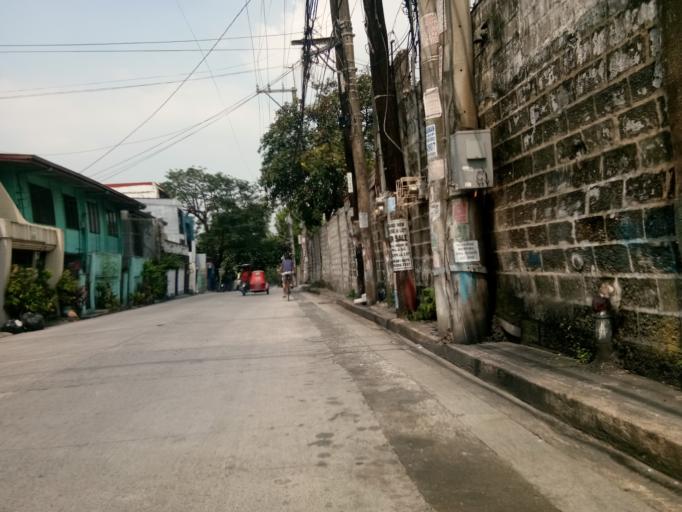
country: PH
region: Metro Manila
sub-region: Marikina
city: Calumpang
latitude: 14.6181
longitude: 121.0624
